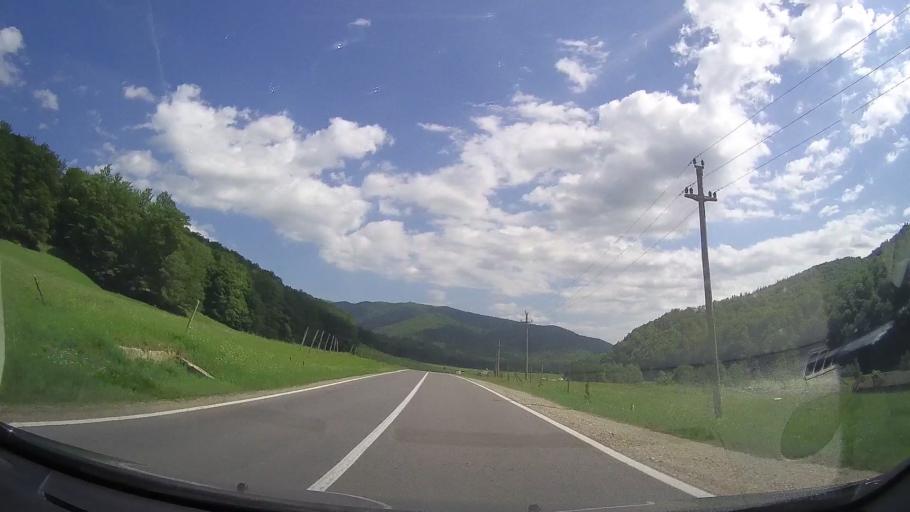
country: RO
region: Prahova
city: Maneciu
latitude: 45.4292
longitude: 25.9394
